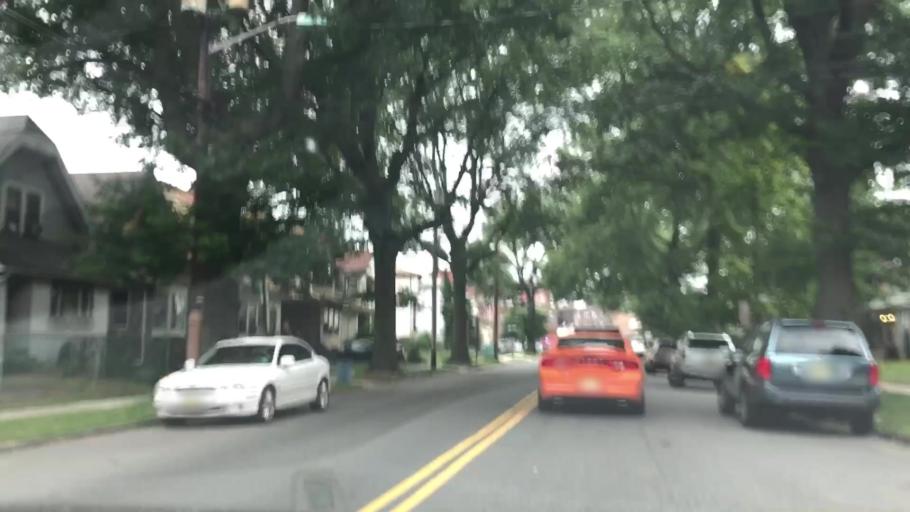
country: US
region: New Jersey
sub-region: Essex County
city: Bloomfield
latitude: 40.7855
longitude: -74.1852
